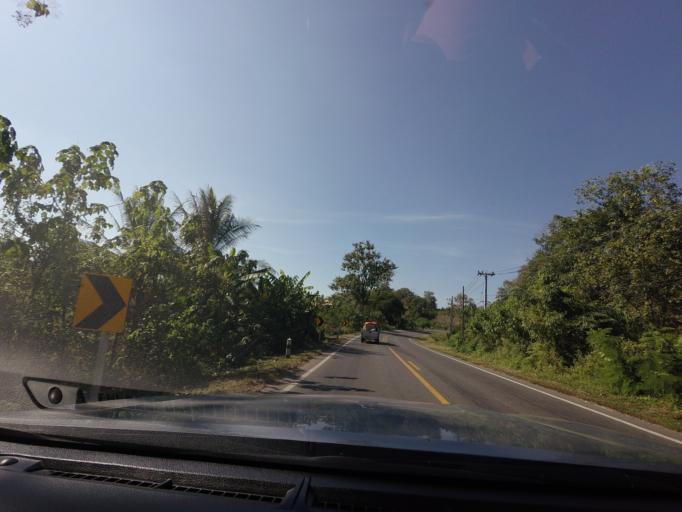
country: TH
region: Sukhothai
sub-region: Amphoe Si Satchanalai
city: Si Satchanalai
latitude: 17.6077
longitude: 99.7079
